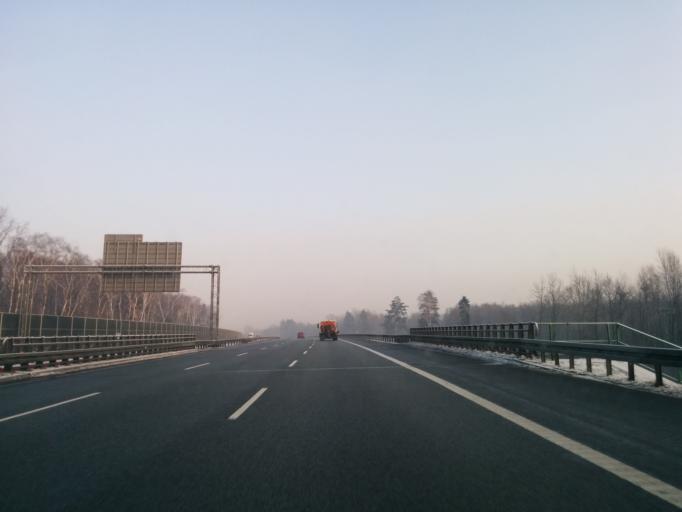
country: PL
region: Silesian Voivodeship
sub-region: Gliwice
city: Gliwice
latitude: 50.3226
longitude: 18.7283
